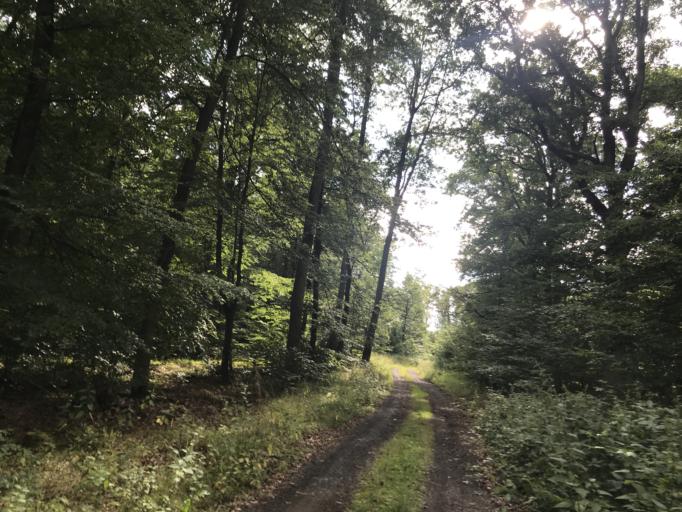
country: DE
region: Hesse
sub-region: Regierungsbezirk Giessen
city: Lohra
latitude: 50.6681
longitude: 8.6140
